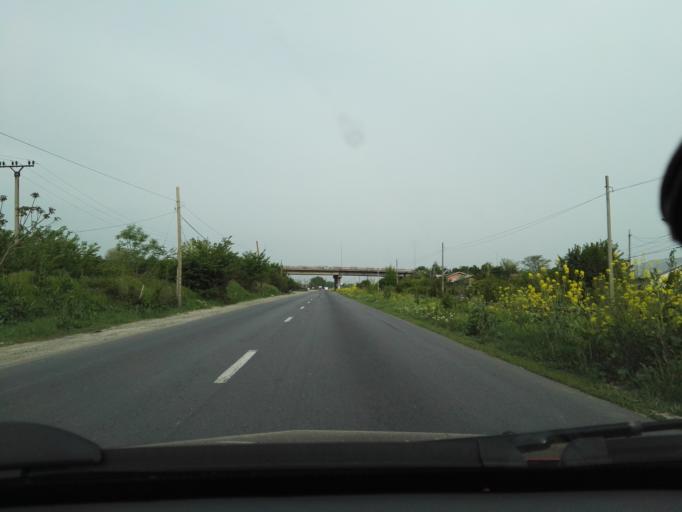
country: RO
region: Ilfov
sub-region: Comuna Magurele
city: Magurele
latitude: 44.3582
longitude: 26.0397
